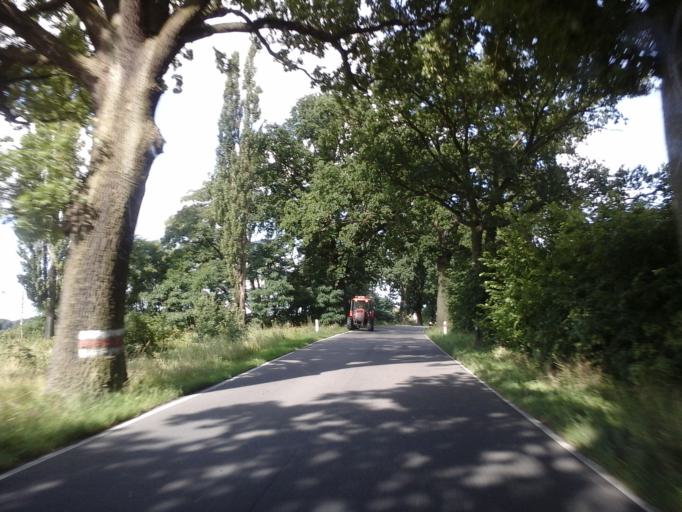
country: PL
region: West Pomeranian Voivodeship
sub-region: Powiat stargardzki
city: Dolice
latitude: 53.1968
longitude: 15.2207
